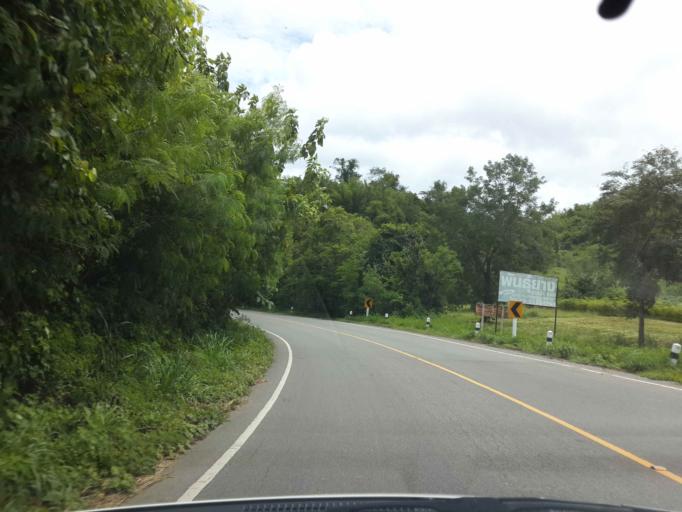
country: TH
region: Ratchaburi
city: Suan Phueng
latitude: 13.5479
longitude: 99.2829
